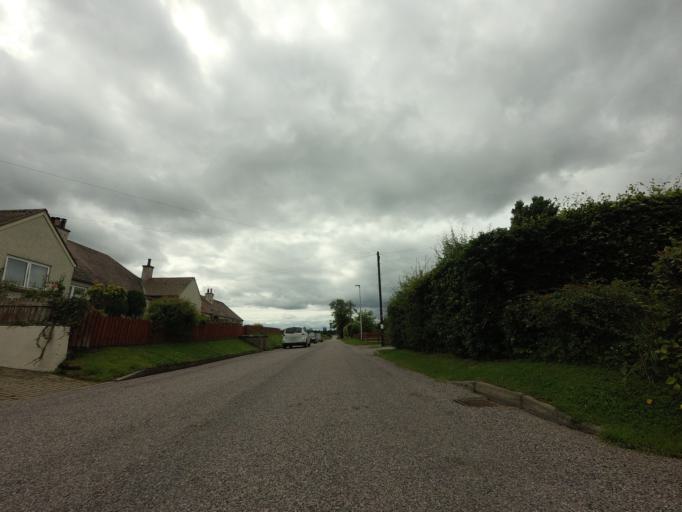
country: GB
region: Scotland
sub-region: Moray
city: Forres
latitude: 57.6025
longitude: -3.6932
